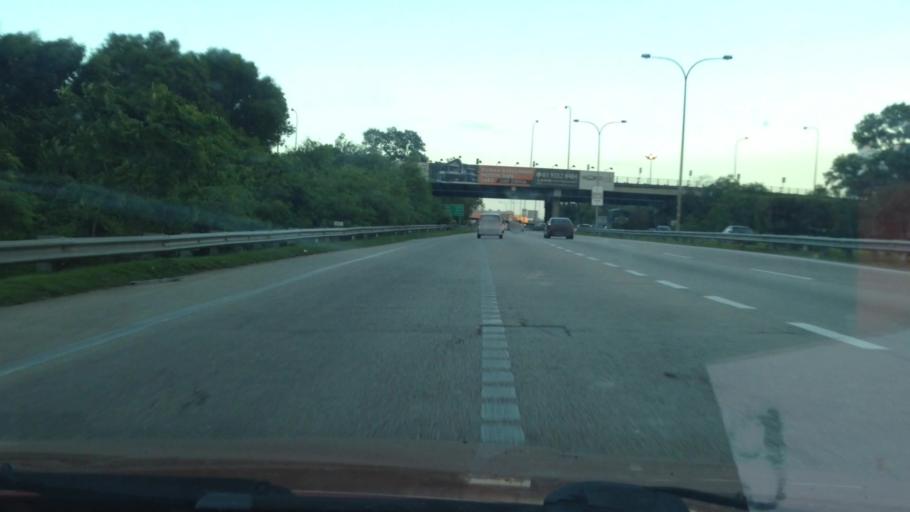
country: MY
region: Selangor
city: Shah Alam
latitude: 3.0957
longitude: 101.5492
